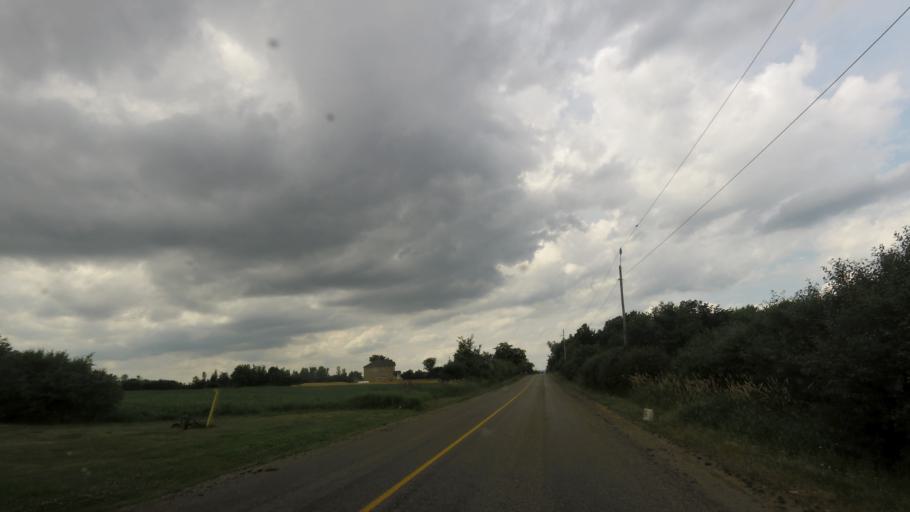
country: CA
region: Ontario
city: Brampton
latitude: 43.7983
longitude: -79.8173
